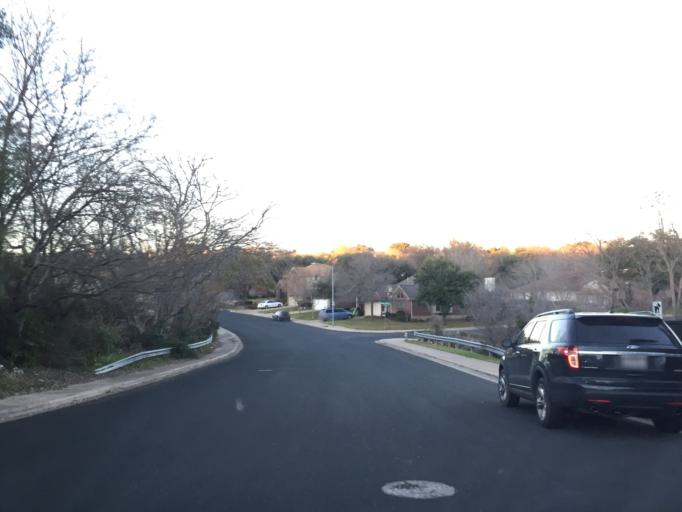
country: US
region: Texas
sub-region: Williamson County
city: Jollyville
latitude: 30.4136
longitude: -97.7634
